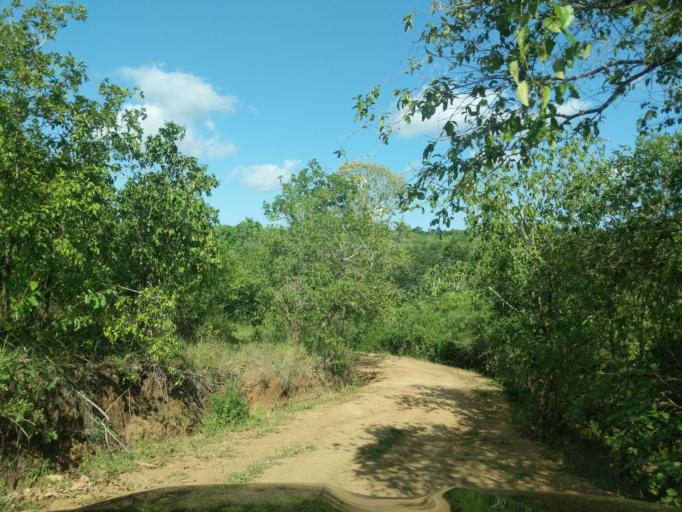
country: TZ
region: Tanga
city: Muheza
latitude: -5.4210
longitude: 38.6477
